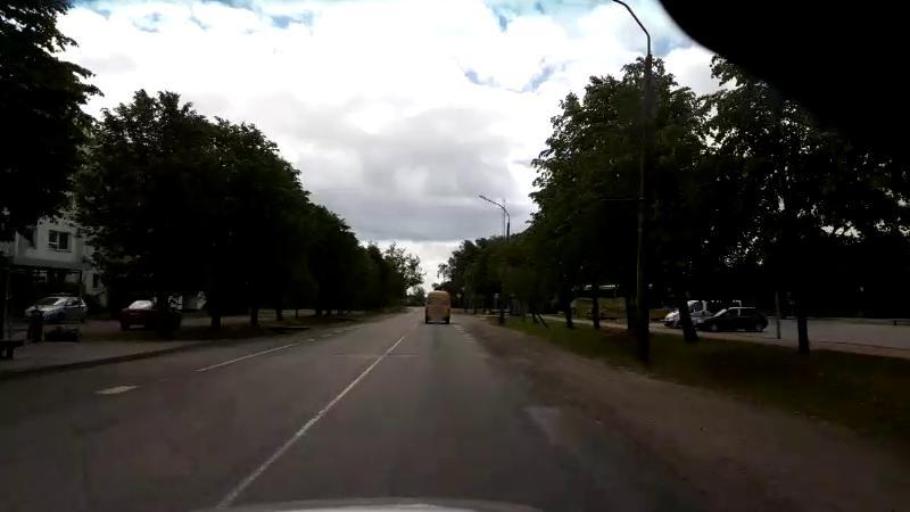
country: LV
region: Salacgrivas
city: Salacgriva
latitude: 57.7489
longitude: 24.3584
